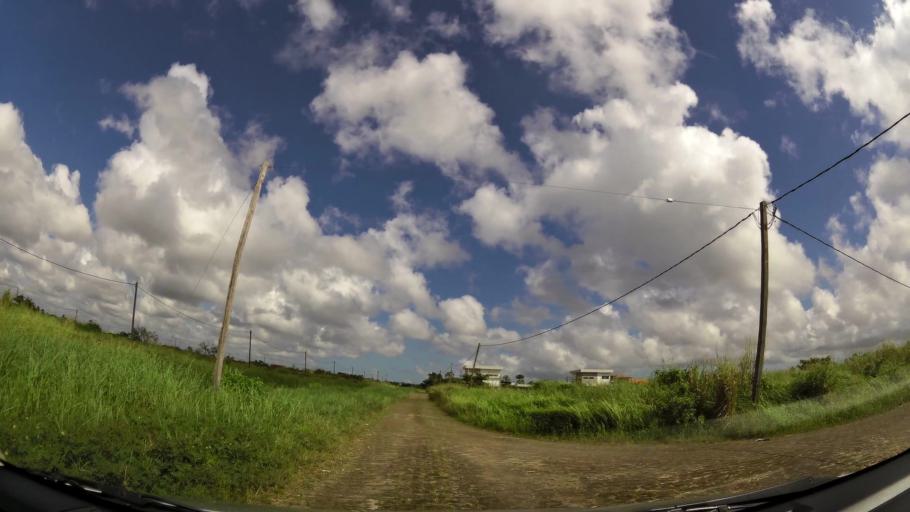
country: SR
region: Paramaribo
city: Paramaribo
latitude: 5.8689
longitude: -55.1245
